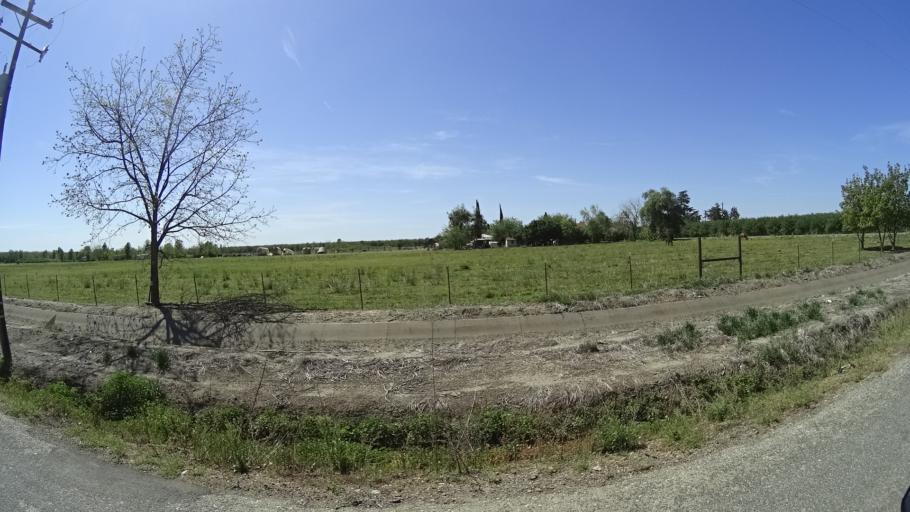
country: US
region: California
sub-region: Glenn County
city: Orland
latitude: 39.7434
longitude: -122.1410
